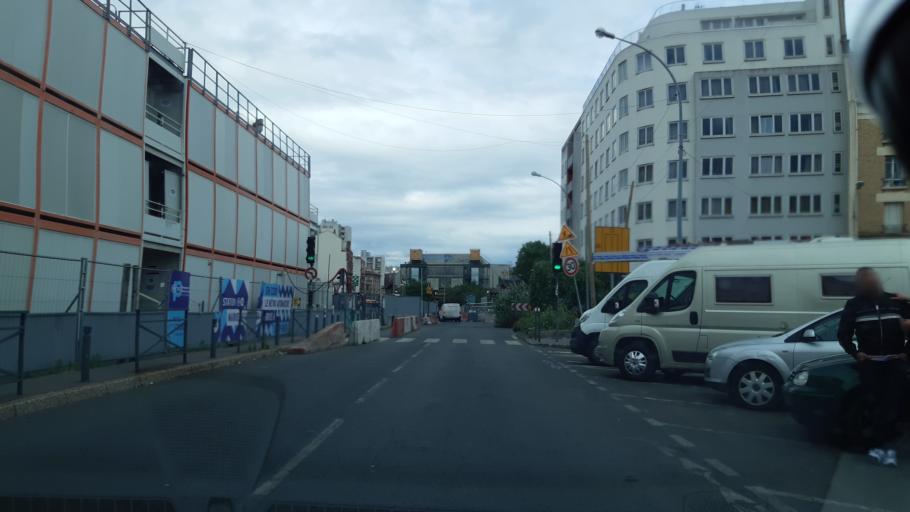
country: FR
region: Ile-de-France
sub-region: Paris
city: Saint-Ouen
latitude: 48.9136
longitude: 2.3333
